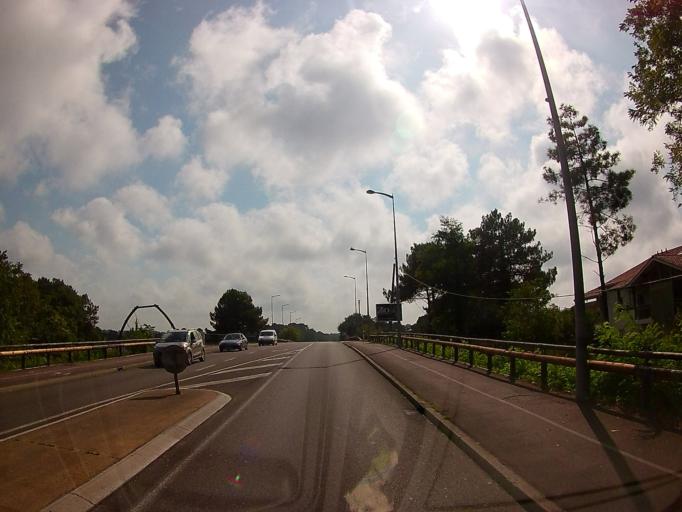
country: FR
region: Aquitaine
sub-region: Departement des Landes
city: Labenne
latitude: 43.5866
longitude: -1.4299
